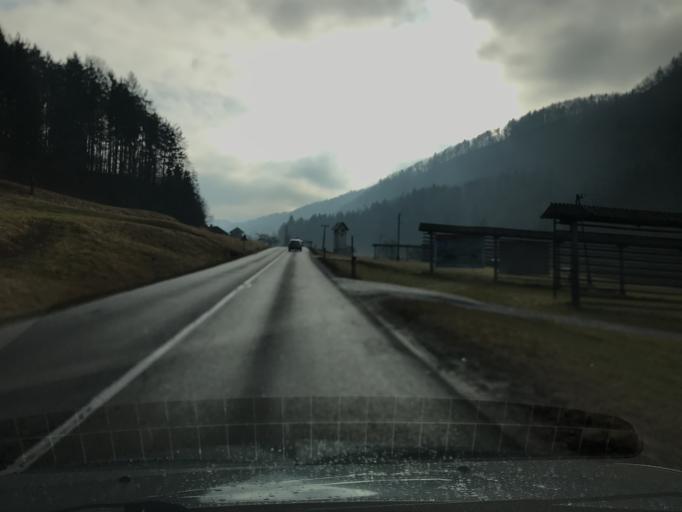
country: SI
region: Kamnik
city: Mekinje
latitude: 46.2268
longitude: 14.6693
